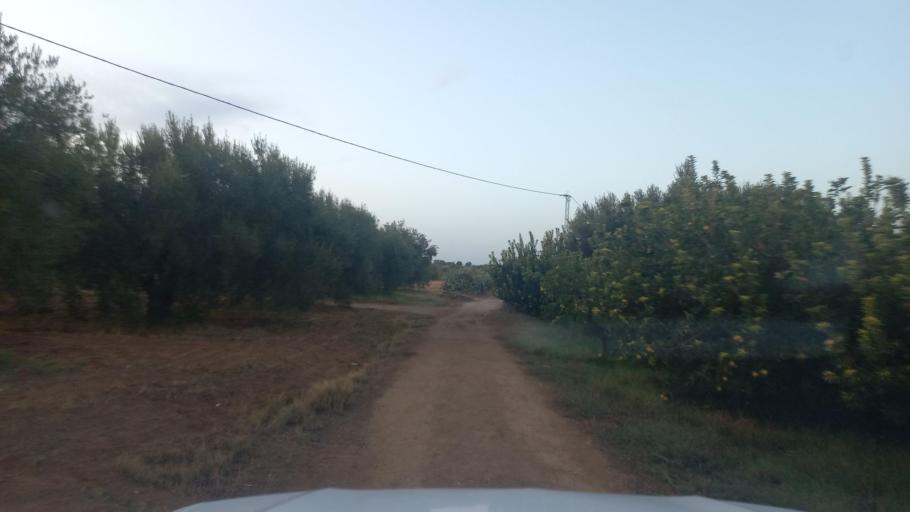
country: TN
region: Al Qasrayn
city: Kasserine
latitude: 35.2229
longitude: 9.0511
